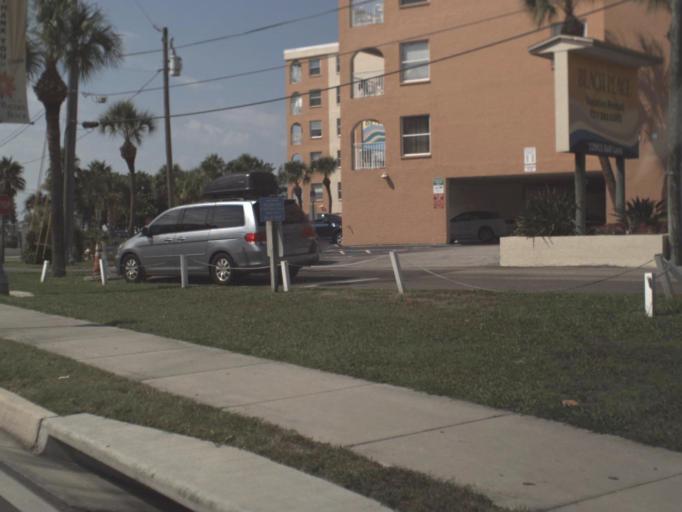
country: US
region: Florida
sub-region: Pinellas County
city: Madeira Beach
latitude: 27.7853
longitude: -82.7835
